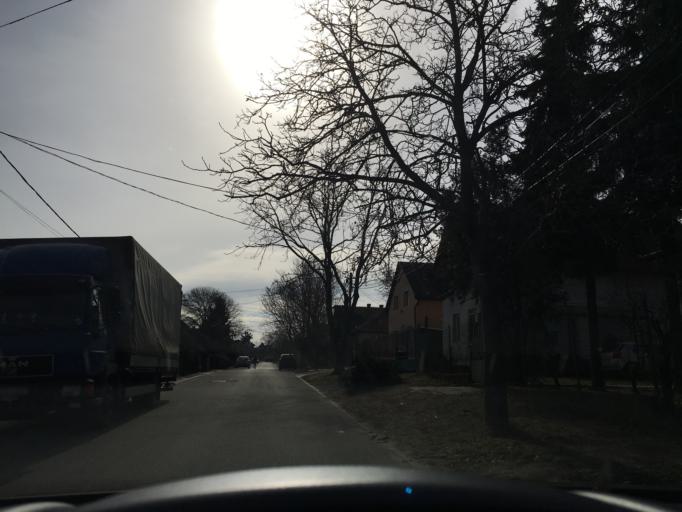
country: HU
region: Budapest
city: Budapest XVII. keruelet
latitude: 47.4780
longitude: 19.2825
